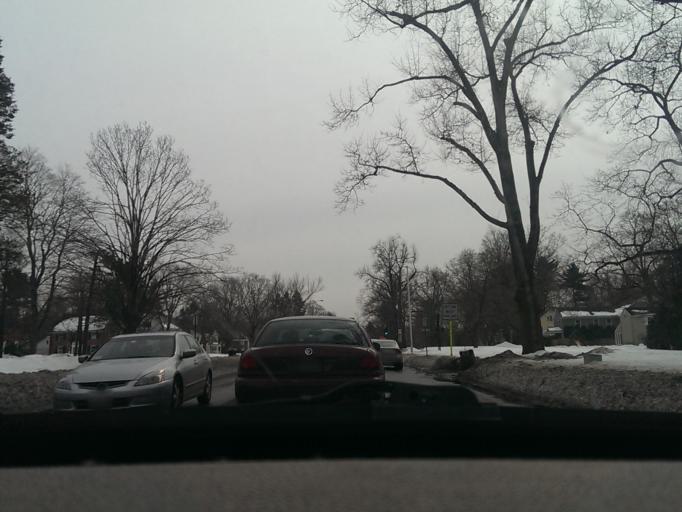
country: US
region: Massachusetts
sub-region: Hampden County
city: Longmeadow
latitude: 42.0661
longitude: -72.5794
